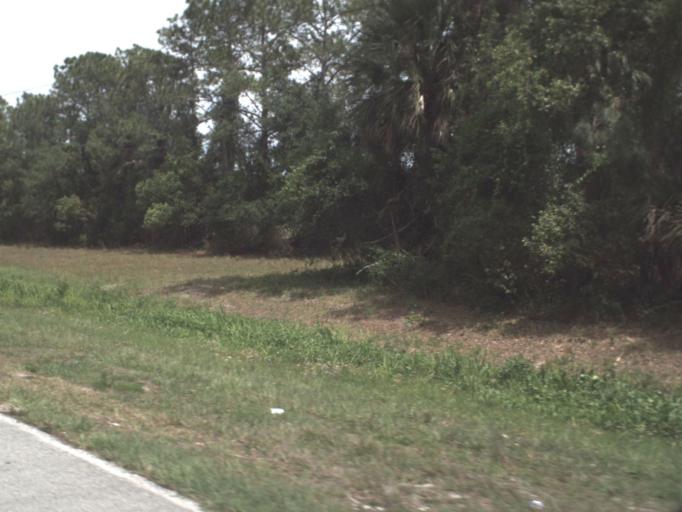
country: US
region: Florida
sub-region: Lake County
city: Lake Mack-Forest Hills
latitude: 28.9973
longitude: -81.3937
